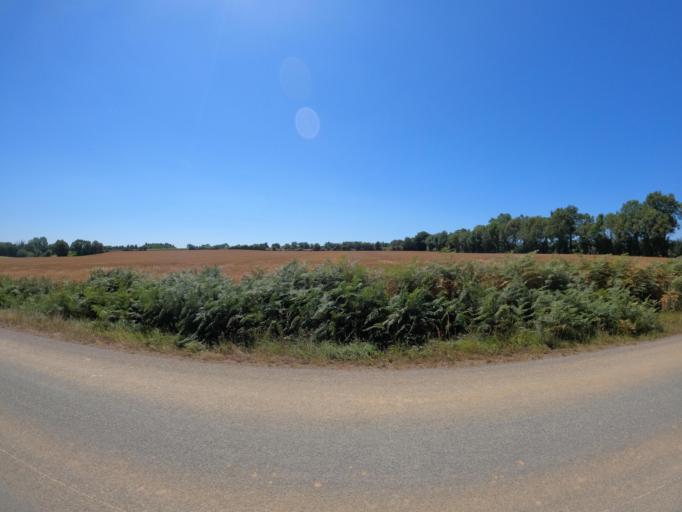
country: FR
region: Pays de la Loire
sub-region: Departement de la Vendee
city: Saint-Philbert-de-Bouaine
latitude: 46.9807
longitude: -1.5283
